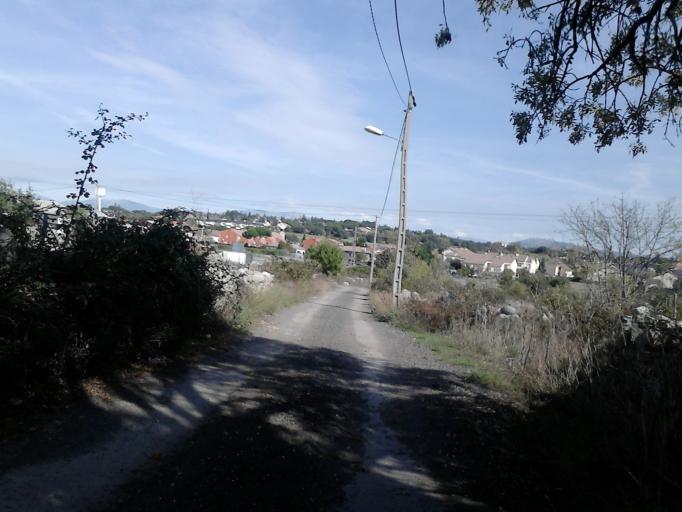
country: ES
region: Madrid
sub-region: Provincia de Madrid
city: Galapagar
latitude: 40.5789
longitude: -3.9947
